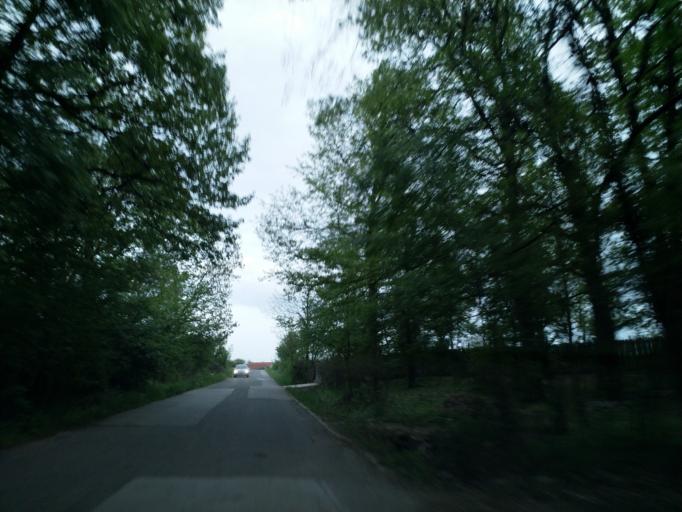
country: RS
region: Central Serbia
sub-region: Pomoravski Okrug
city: Paracin
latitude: 43.9487
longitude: 21.4902
